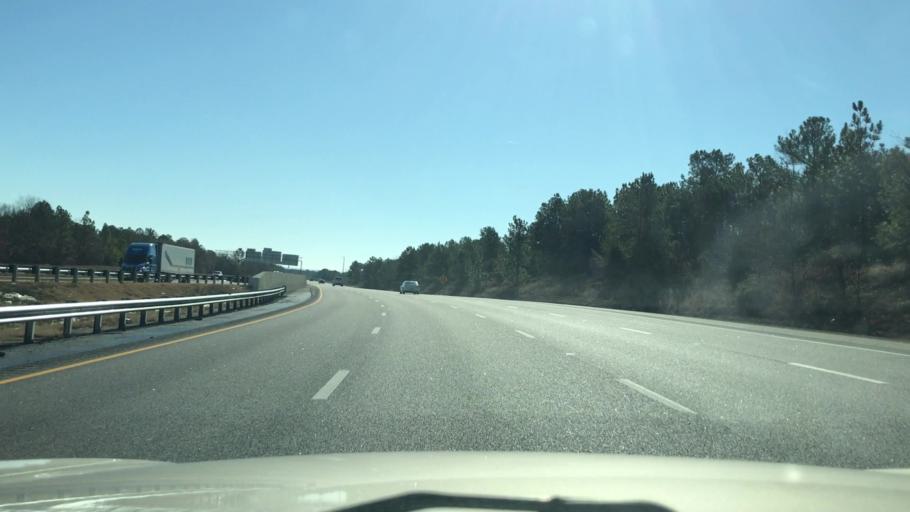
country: US
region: South Carolina
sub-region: Lexington County
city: Pineridge
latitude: 33.9210
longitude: -81.0673
